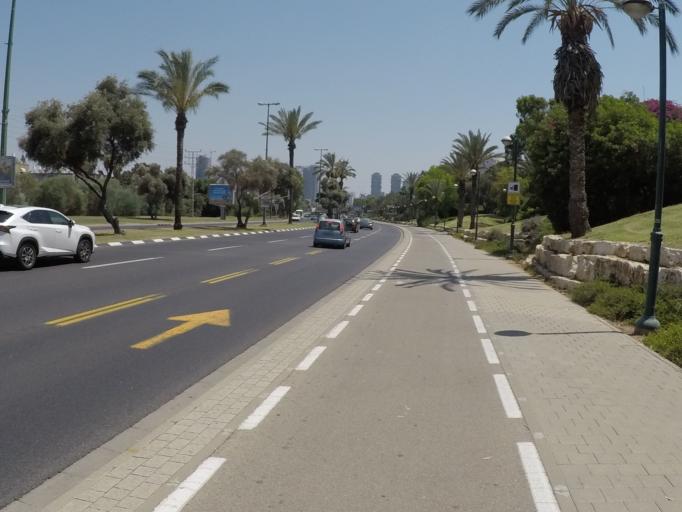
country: IL
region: Tel Aviv
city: Tel Aviv
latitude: 32.1079
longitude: 34.7918
